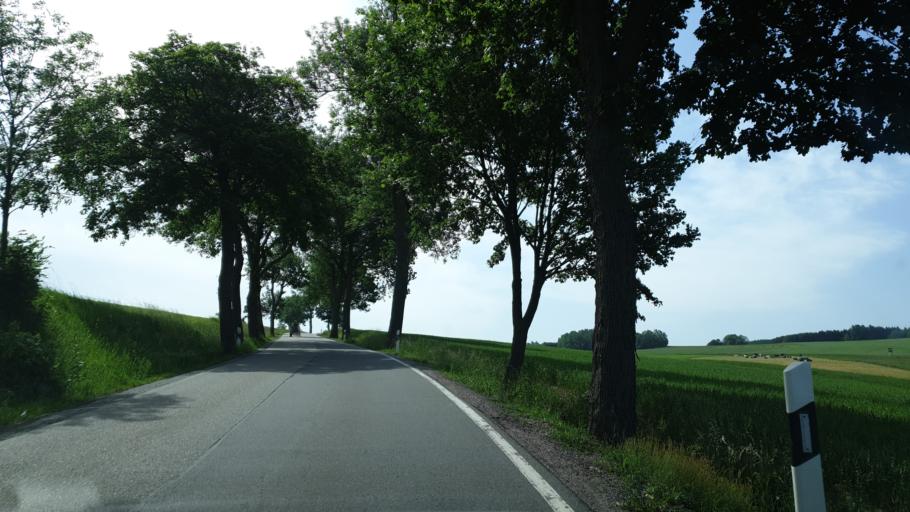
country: DE
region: Saxony
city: Zschorlau
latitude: 50.5591
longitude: 12.6457
